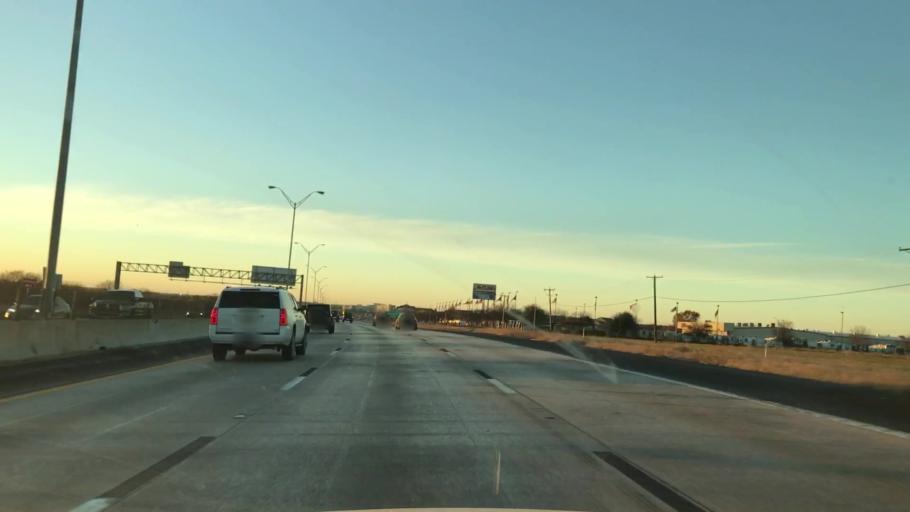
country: US
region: Texas
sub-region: Tarrant County
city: Everman
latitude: 32.6117
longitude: -97.3215
